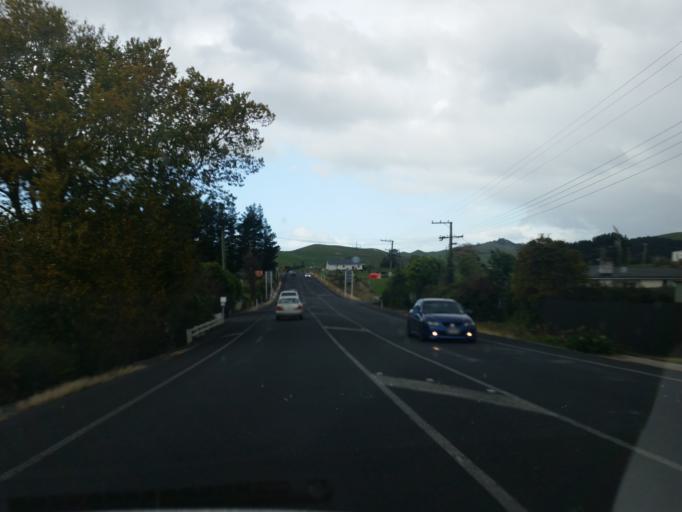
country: NZ
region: Waikato
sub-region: Waikato District
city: Te Kauwhata
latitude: -37.2506
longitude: 175.2289
